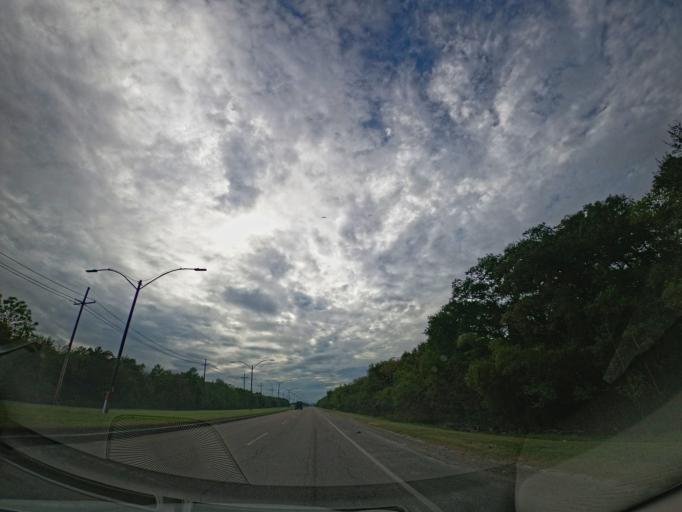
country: US
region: Louisiana
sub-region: Saint Bernard Parish
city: Arabi
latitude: 30.0068
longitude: -90.0017
